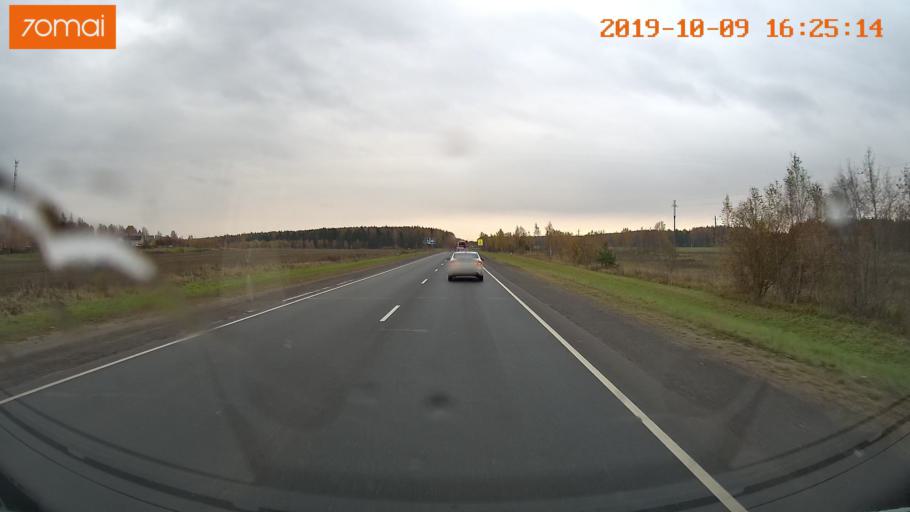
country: RU
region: Kostroma
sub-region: Kostromskoy Rayon
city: Kostroma
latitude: 57.6442
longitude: 40.9180
